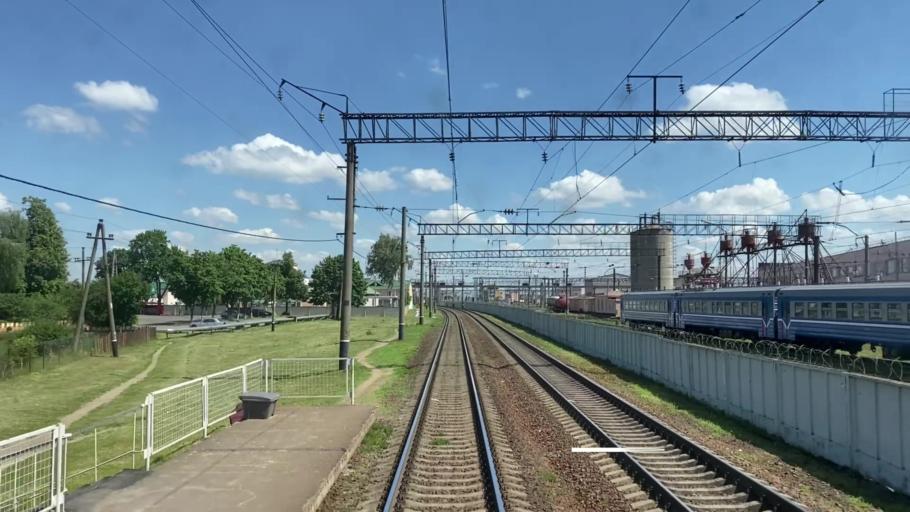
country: BY
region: Brest
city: Baranovichi
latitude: 53.1205
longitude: 25.9723
